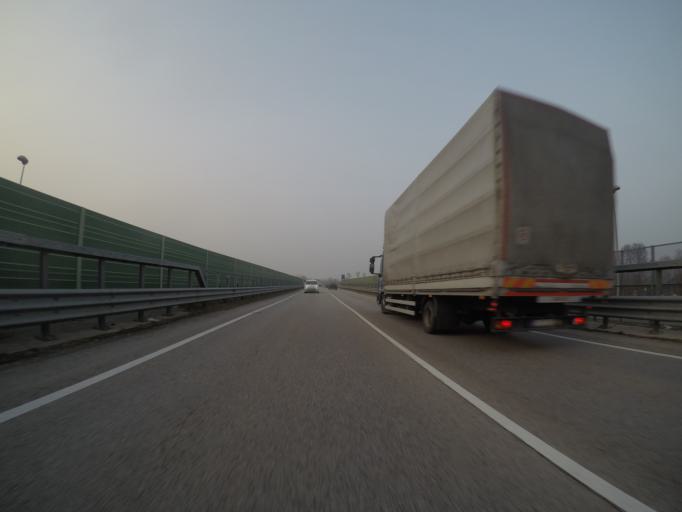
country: IT
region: Veneto
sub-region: Provincia di Treviso
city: Resana
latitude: 45.6317
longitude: 11.9354
